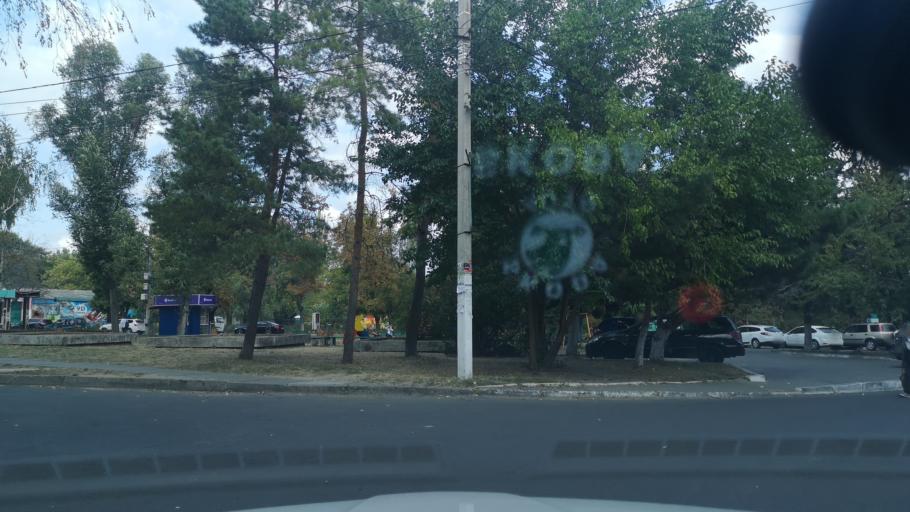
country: MD
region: Chisinau
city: Chisinau
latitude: 46.9980
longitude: 28.8523
